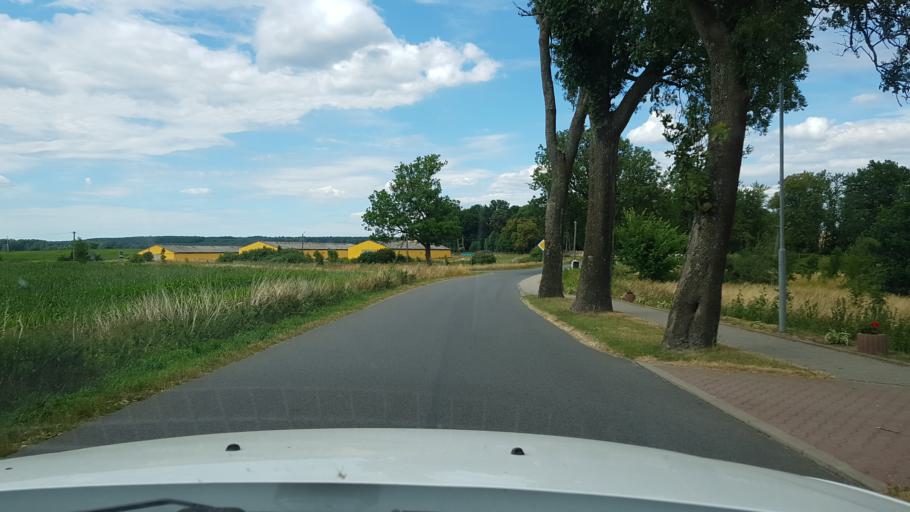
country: PL
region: West Pomeranian Voivodeship
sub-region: Powiat drawski
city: Kalisz Pomorski
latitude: 53.3347
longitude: 15.9318
